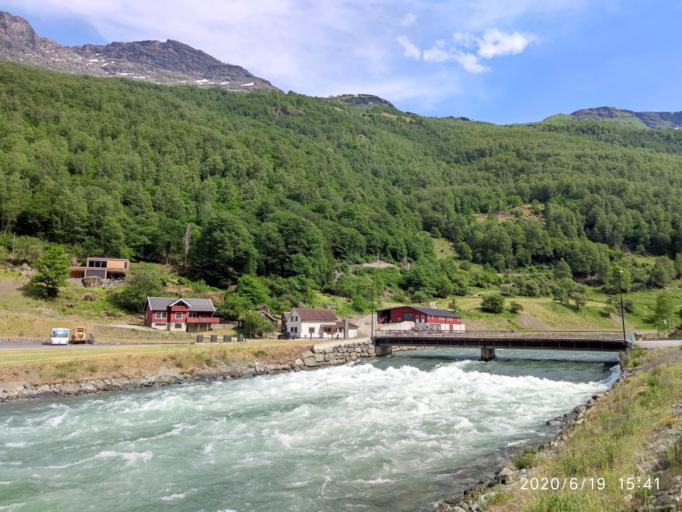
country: NO
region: Sogn og Fjordane
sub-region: Aurland
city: Aurlandsvangen
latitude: 60.8373
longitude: 7.1203
